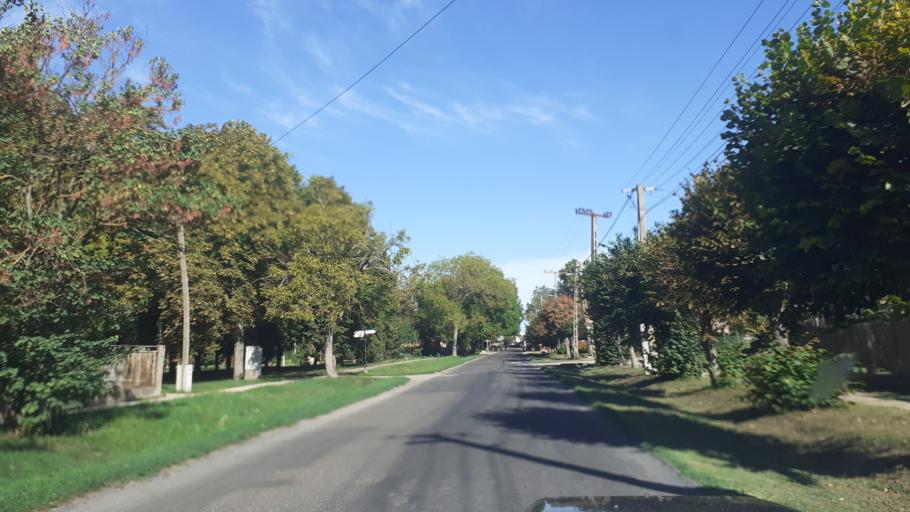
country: HU
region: Fejer
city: Ivancsa
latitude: 47.1895
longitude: 18.7959
